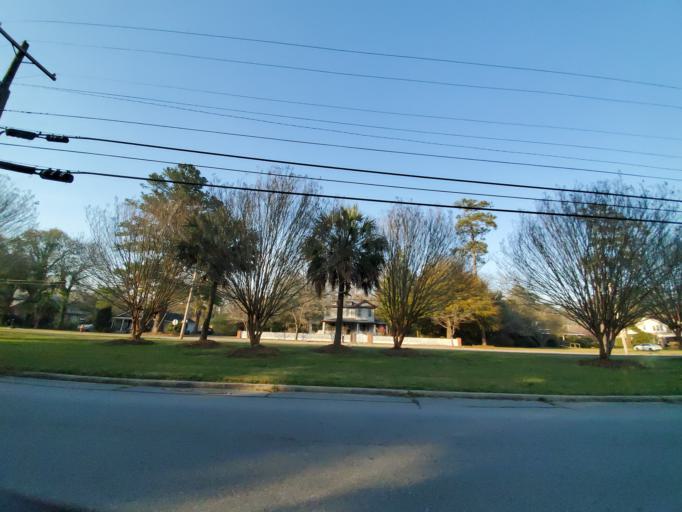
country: US
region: South Carolina
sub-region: Bamberg County
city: Bamberg
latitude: 33.2950
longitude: -81.0273
